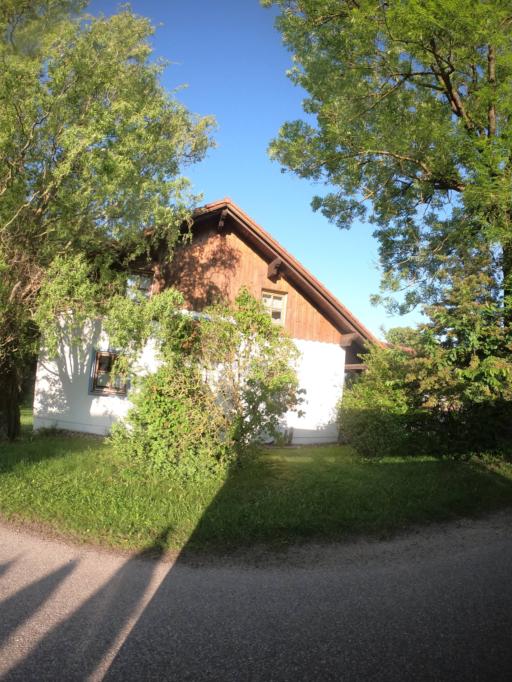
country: DE
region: Bavaria
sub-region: Upper Bavaria
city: Inning am Holz
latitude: 48.3475
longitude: 12.0779
